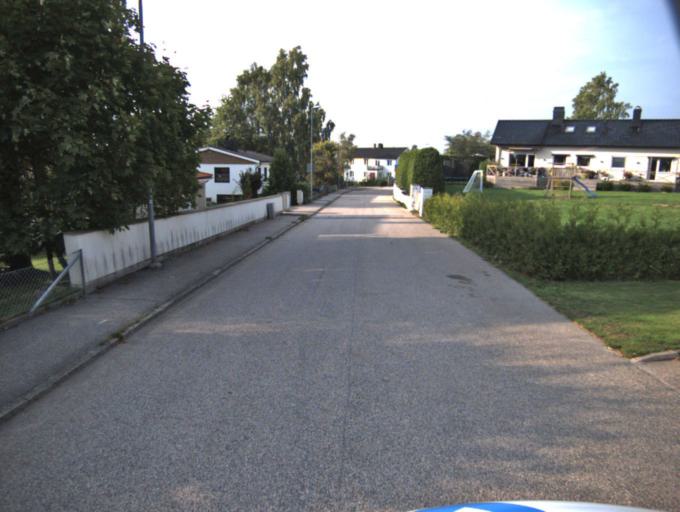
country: SE
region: Vaestra Goetaland
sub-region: Ulricehamns Kommun
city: Ulricehamn
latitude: 57.7840
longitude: 13.4227
